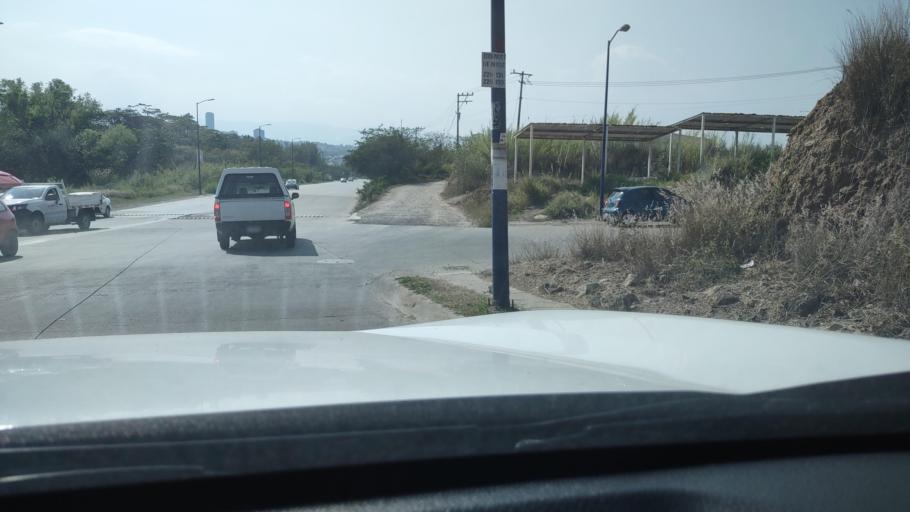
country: MX
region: Veracruz
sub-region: Emiliano Zapata
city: Las Trancas
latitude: 19.5129
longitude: -96.8520
